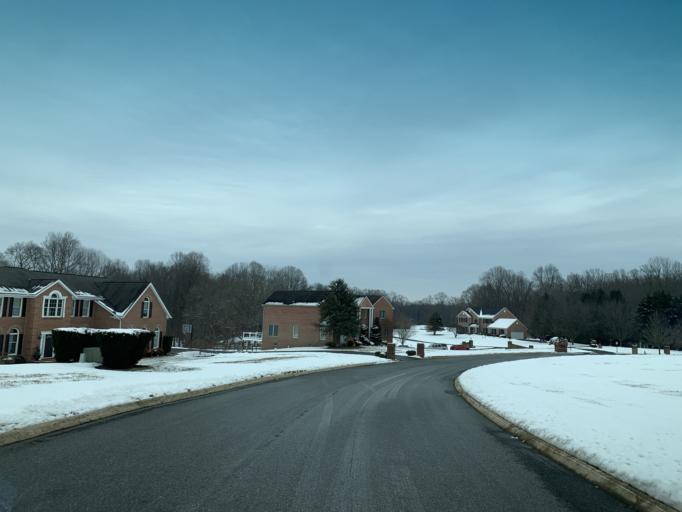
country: US
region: Maryland
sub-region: Harford County
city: Jarrettsville
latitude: 39.5843
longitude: -76.4637
